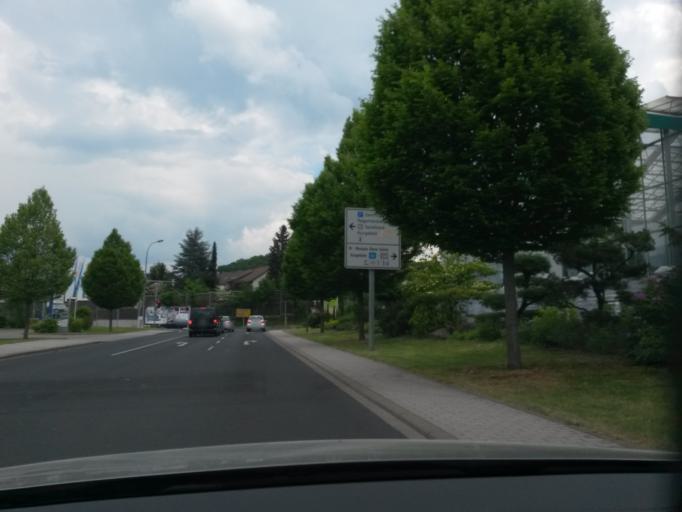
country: DE
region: Bavaria
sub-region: Regierungsbezirk Unterfranken
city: Bad Kissingen
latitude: 50.1907
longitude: 10.0623
